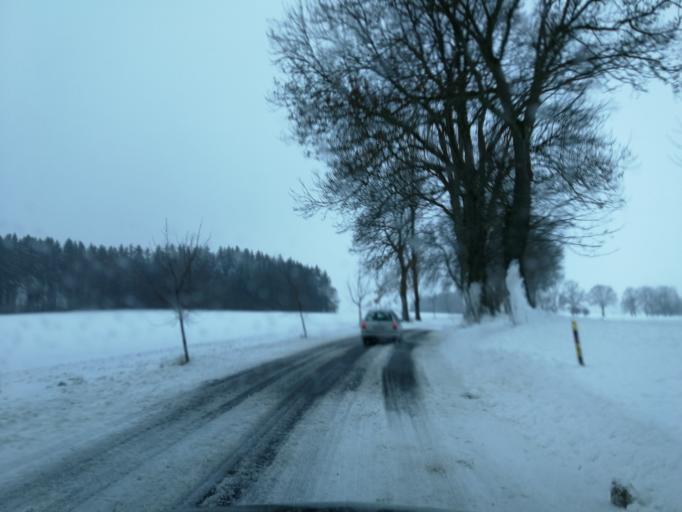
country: CZ
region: Vysocina
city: Heralec
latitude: 49.5334
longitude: 15.4379
